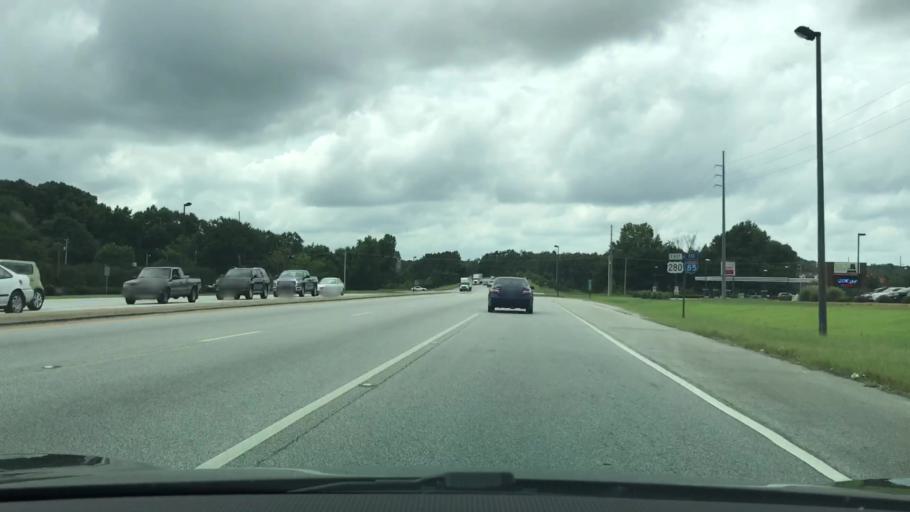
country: US
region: Alabama
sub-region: Lee County
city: Opelika
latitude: 32.6374
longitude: -85.4098
